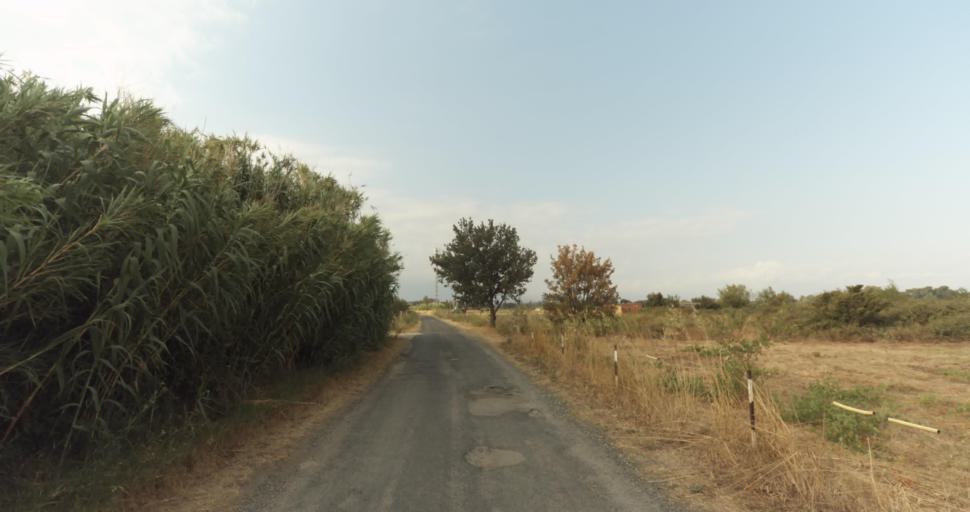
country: FR
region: Languedoc-Roussillon
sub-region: Departement des Pyrenees-Orientales
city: Villeneuve-de-la-Raho
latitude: 42.6274
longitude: 2.9313
